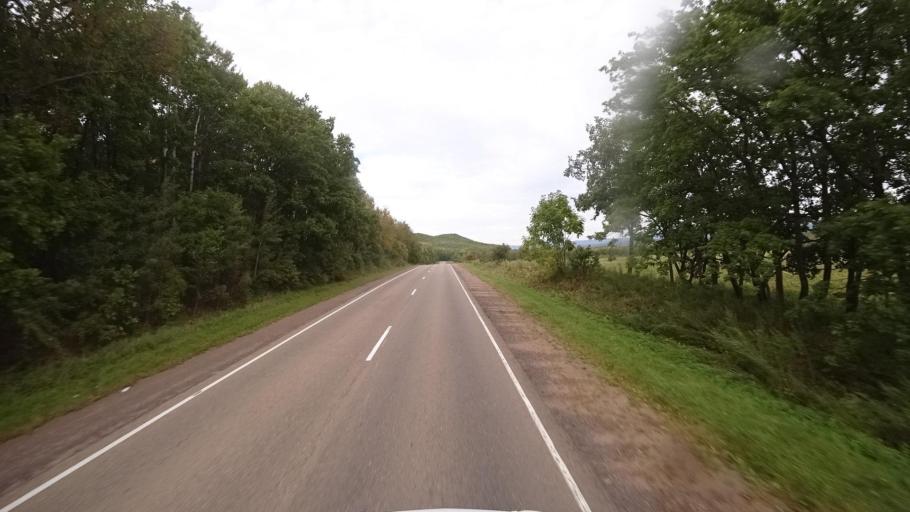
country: RU
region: Primorskiy
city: Yakovlevka
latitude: 44.3746
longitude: 133.4406
